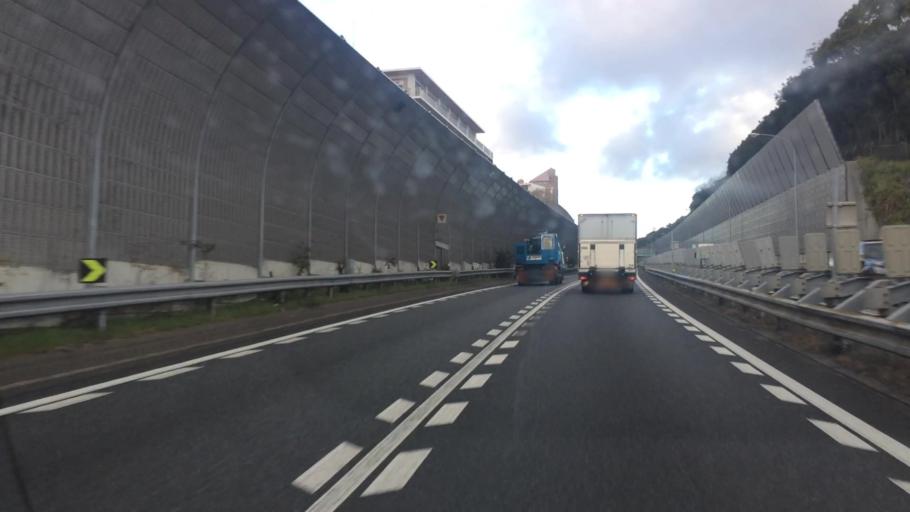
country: JP
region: Hyogo
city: Akashi
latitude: 34.6538
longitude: 135.0362
